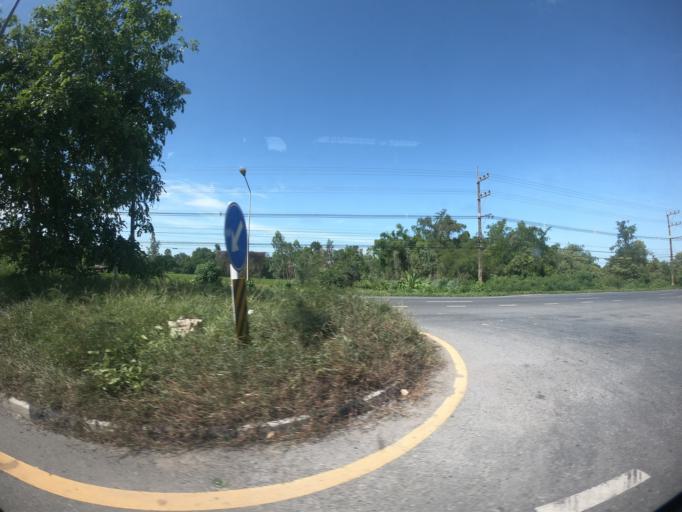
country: TH
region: Nakhon Nayok
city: Ban Na
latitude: 14.2420
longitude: 101.1180
